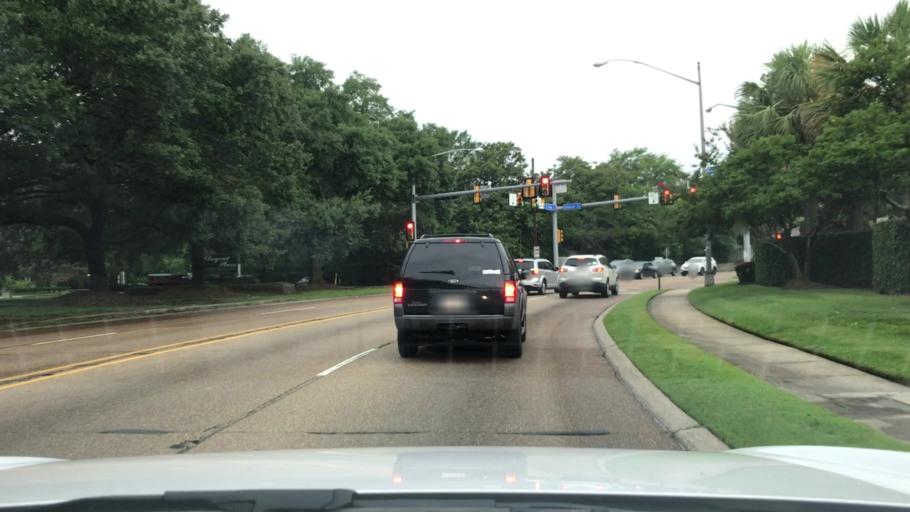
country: US
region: Louisiana
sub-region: East Baton Rouge Parish
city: Baton Rouge
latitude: 30.4410
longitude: -91.1378
